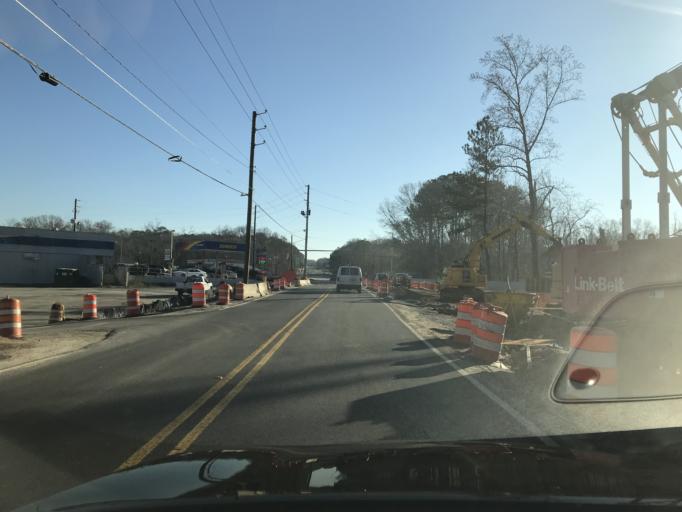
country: US
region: Georgia
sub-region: Clayton County
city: Jonesboro
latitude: 33.5181
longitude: -84.3819
